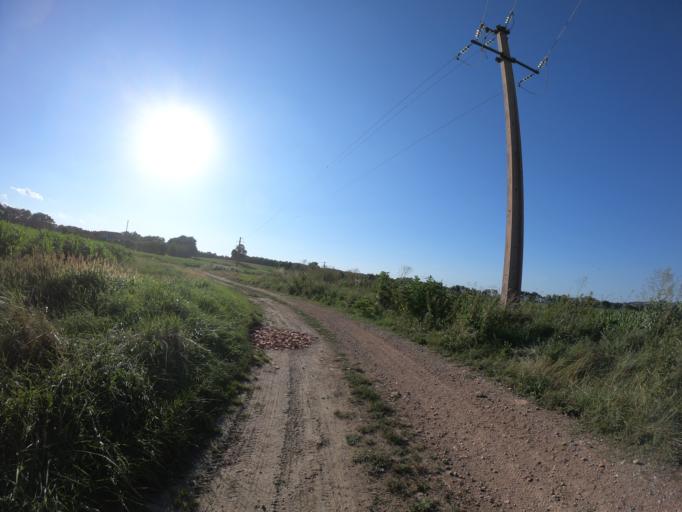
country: FR
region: Midi-Pyrenees
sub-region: Departement de l'Ariege
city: La Tour-du-Crieu
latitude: 43.1021
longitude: 1.7319
